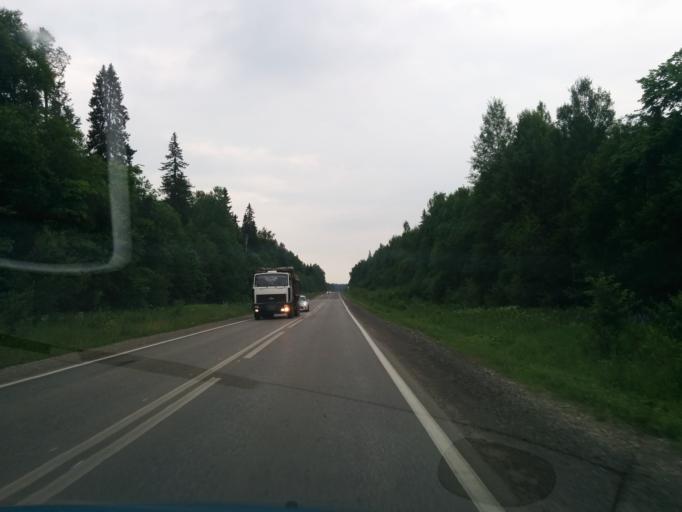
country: RU
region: Perm
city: Perm
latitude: 58.1830
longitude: 56.2228
